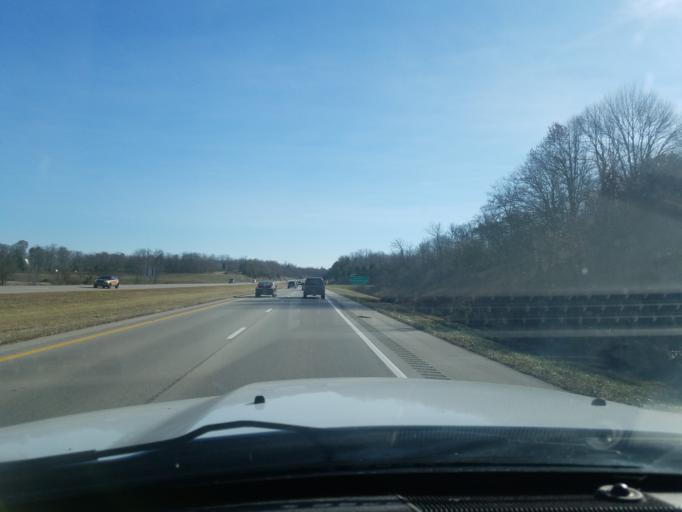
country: US
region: Ohio
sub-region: Brown County
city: Mount Orab
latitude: 39.0136
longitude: -83.8010
